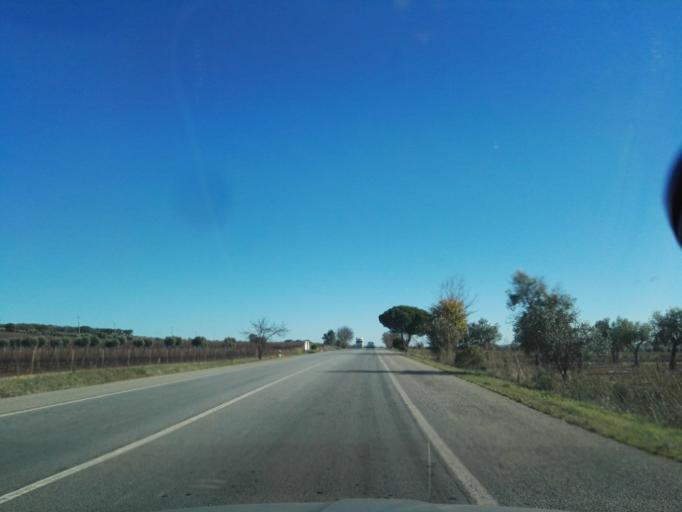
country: PT
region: Evora
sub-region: Estremoz
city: Estremoz
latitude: 38.8321
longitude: -7.5401
